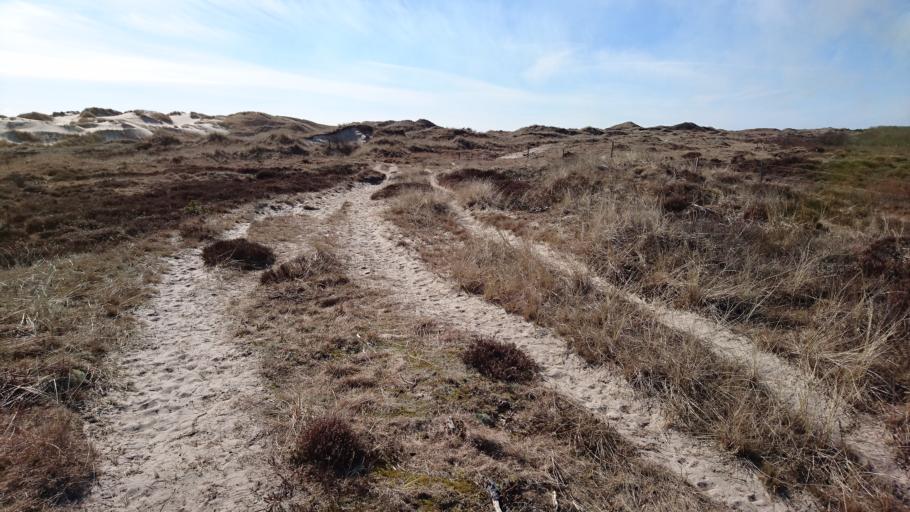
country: DK
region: North Denmark
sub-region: Frederikshavn Kommune
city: Strandby
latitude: 57.6534
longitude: 10.4035
